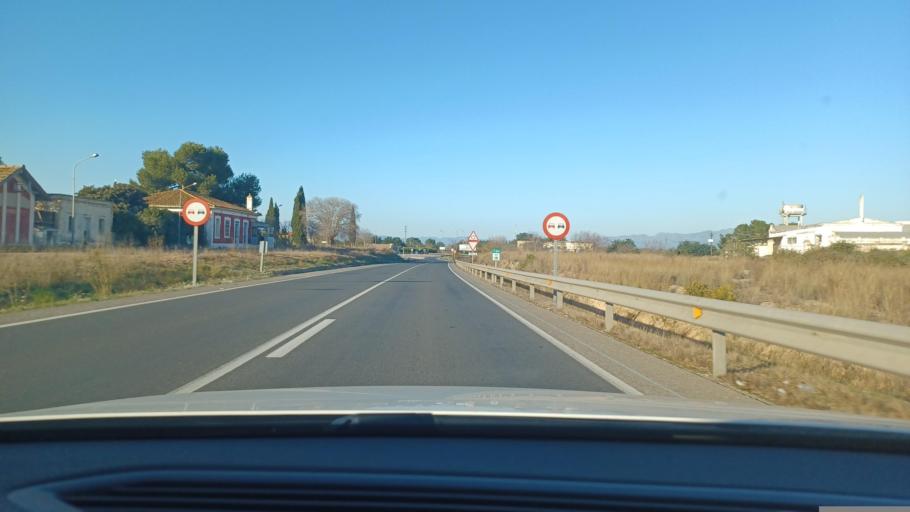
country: ES
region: Catalonia
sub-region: Provincia de Tarragona
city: Santa Barbara
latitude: 40.7146
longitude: 0.5062
